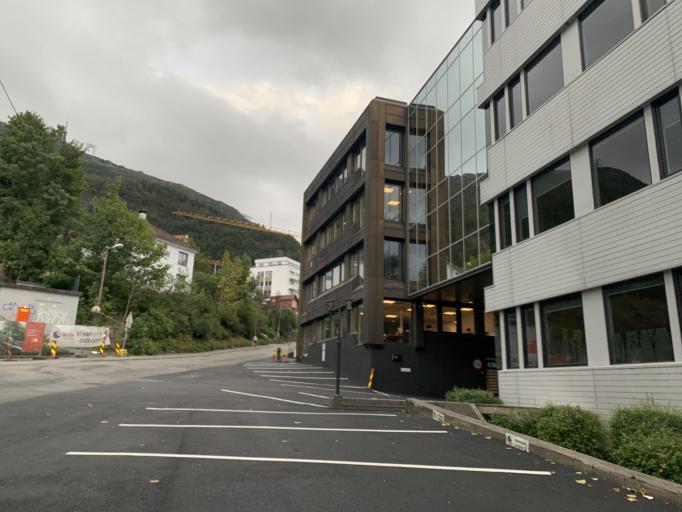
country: NO
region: Hordaland
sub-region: Bergen
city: Bergen
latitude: 60.3778
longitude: 5.3557
